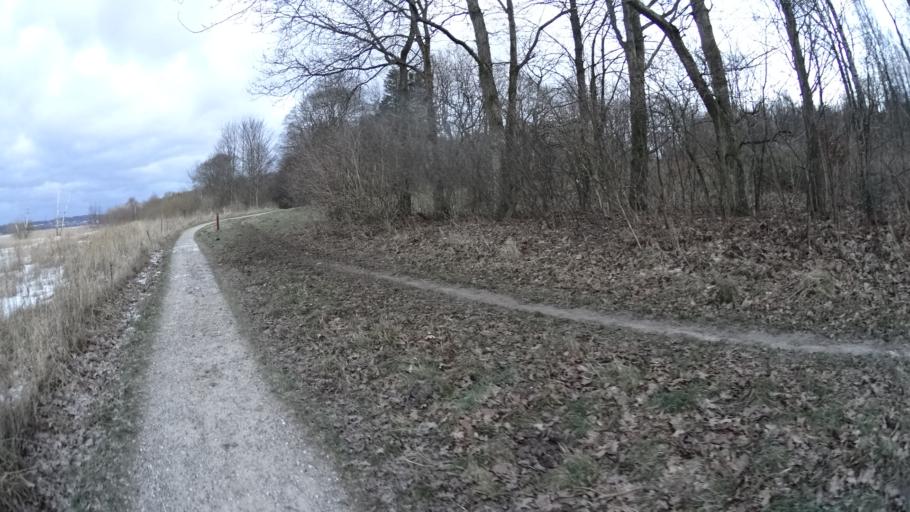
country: DK
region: Central Jutland
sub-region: Arhus Kommune
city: Kolt
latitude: 56.1358
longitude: 10.0679
